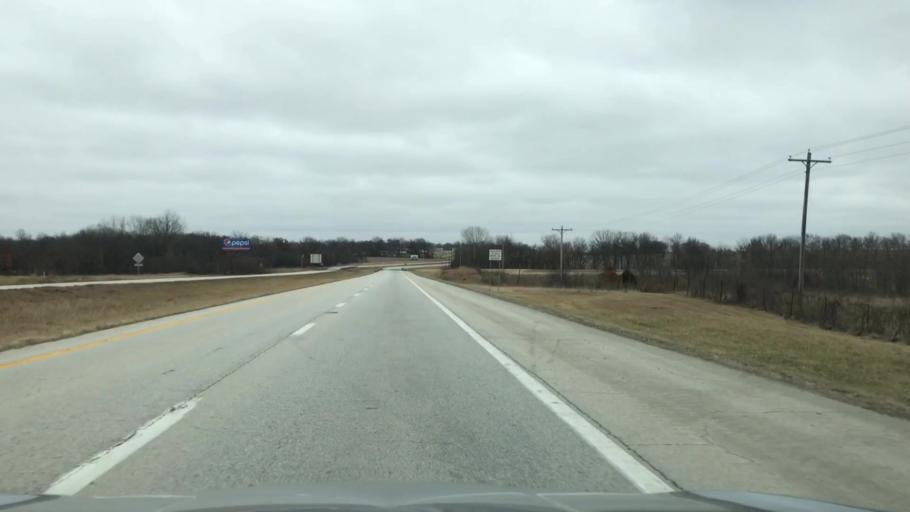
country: US
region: Missouri
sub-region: Livingston County
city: Chillicothe
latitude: 39.7738
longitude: -93.5351
